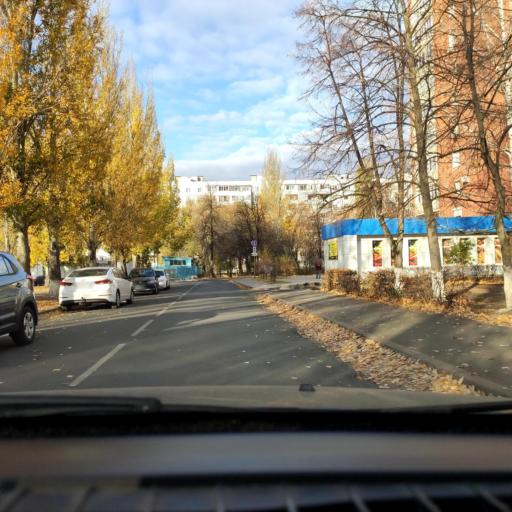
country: RU
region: Samara
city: Tol'yatti
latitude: 53.5247
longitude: 49.2872
